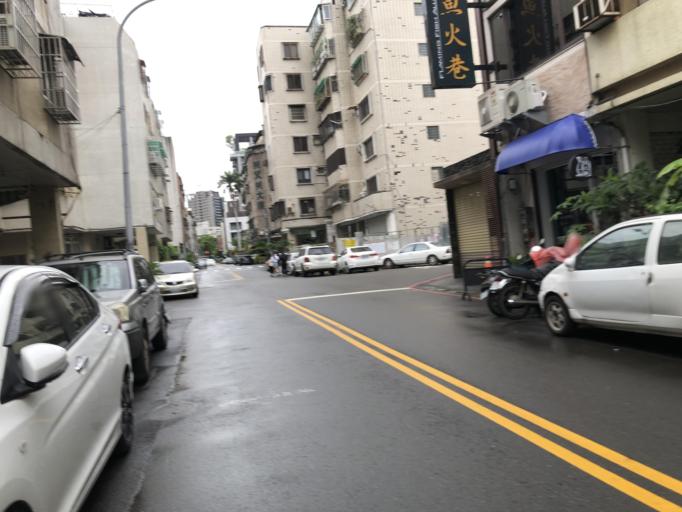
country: TW
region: Taiwan
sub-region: Taichung City
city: Taichung
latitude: 24.1485
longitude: 120.6676
